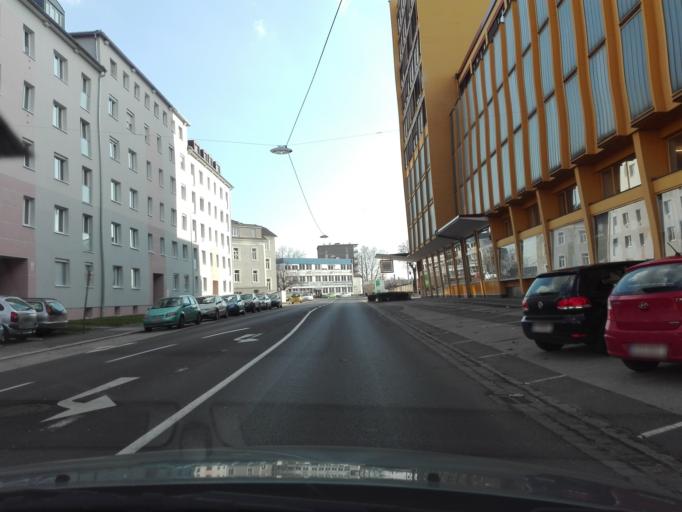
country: AT
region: Upper Austria
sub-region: Linz Stadt
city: Linz
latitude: 48.2904
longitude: 14.3056
